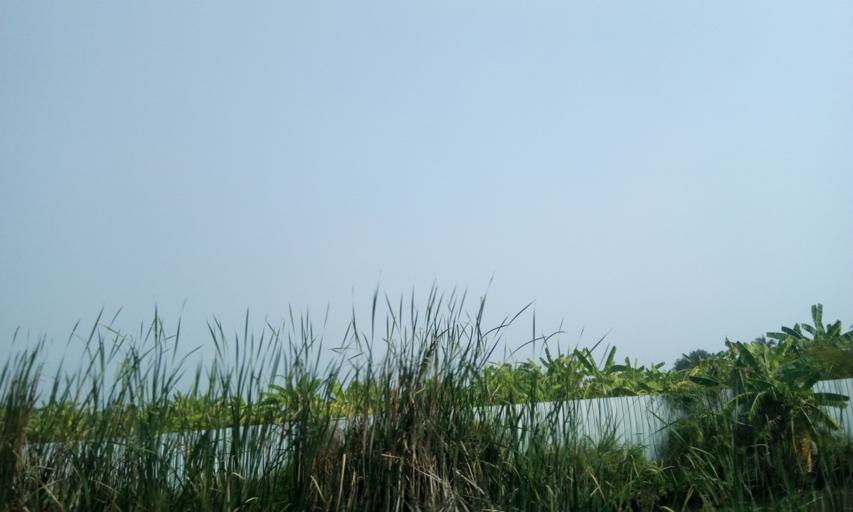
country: TH
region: Pathum Thani
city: Lam Luk Ka
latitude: 13.9413
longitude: 100.7242
